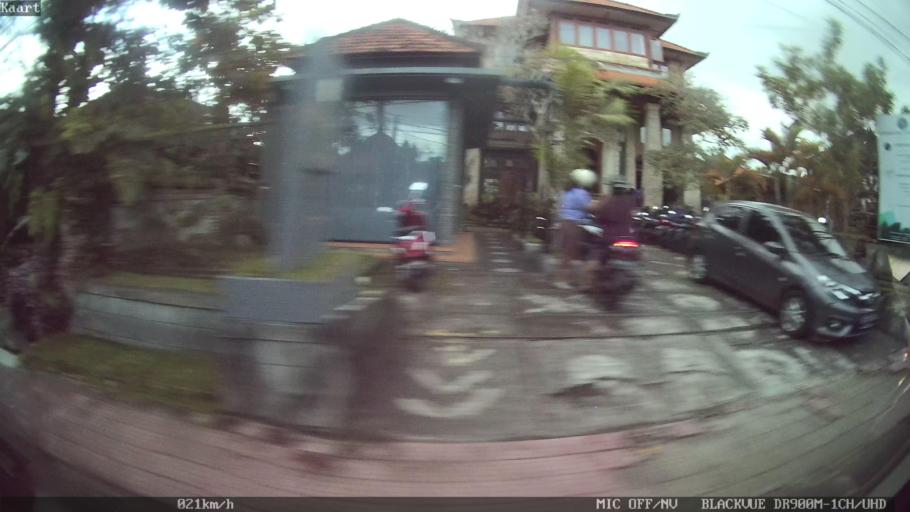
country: ID
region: Bali
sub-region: Kabupaten Gianyar
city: Ubud
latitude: -8.4975
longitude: 115.2533
